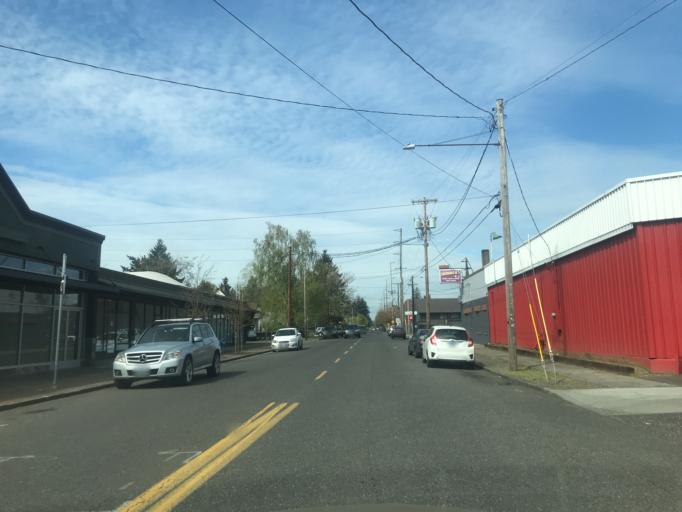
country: US
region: Oregon
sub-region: Multnomah County
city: Lents
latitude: 45.4831
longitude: -122.5802
